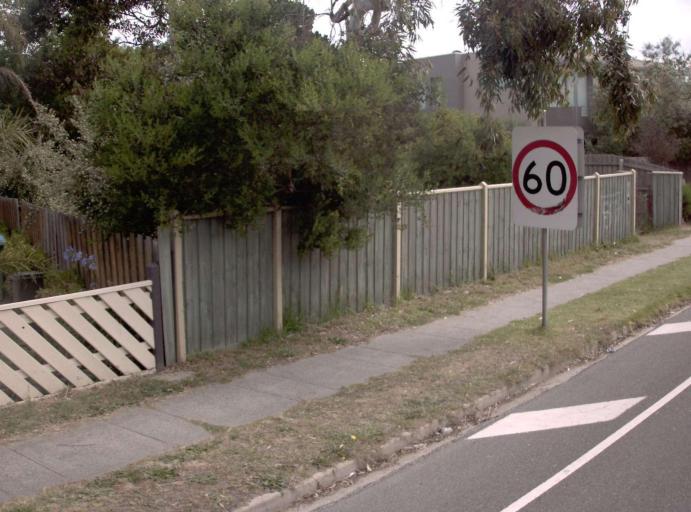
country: AU
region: Victoria
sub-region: Mornington Peninsula
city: Rosebud West
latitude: -38.3643
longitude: 144.8735
